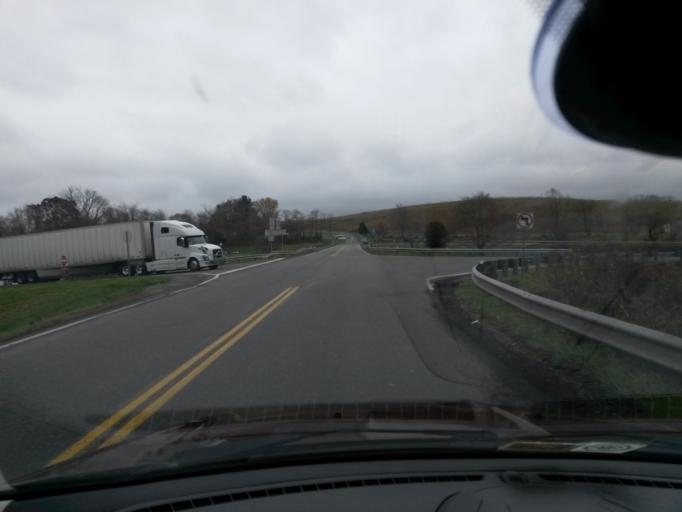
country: US
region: Virginia
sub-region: Pulaski County
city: Pulaski
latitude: 36.9513
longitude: -80.8817
